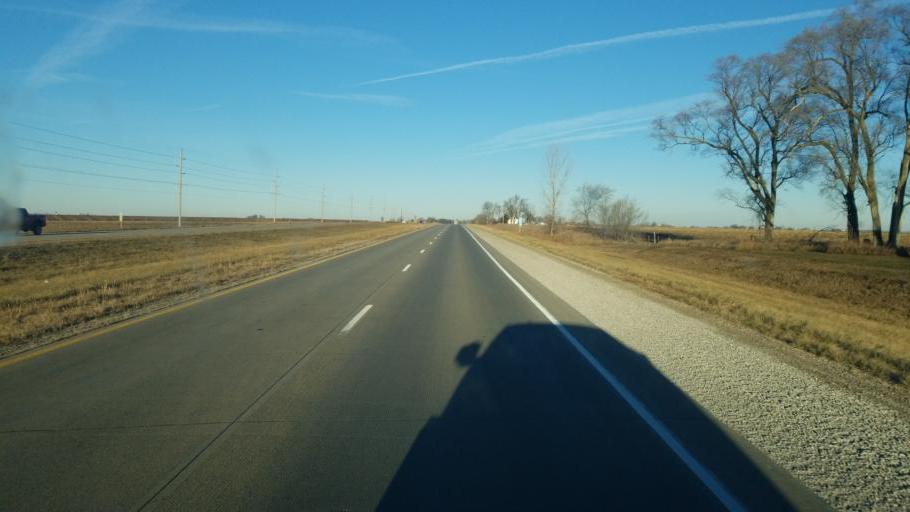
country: US
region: Iowa
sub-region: Mahaska County
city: Oskaloosa
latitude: 41.3400
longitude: -92.7367
